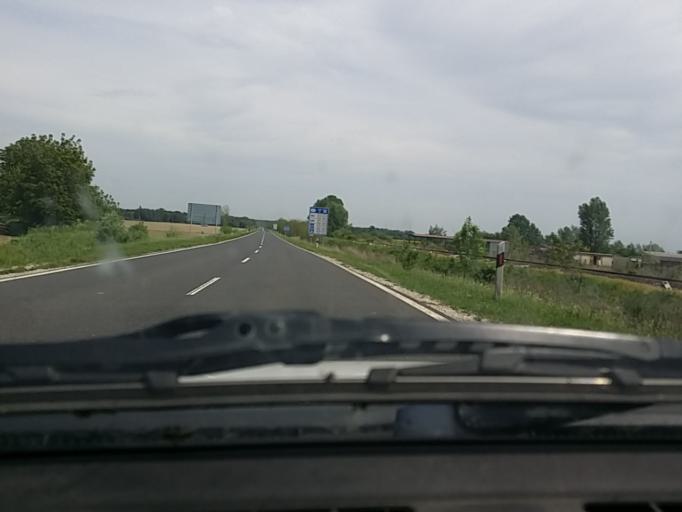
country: HU
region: Somogy
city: Barcs
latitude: 45.9519
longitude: 17.4695
